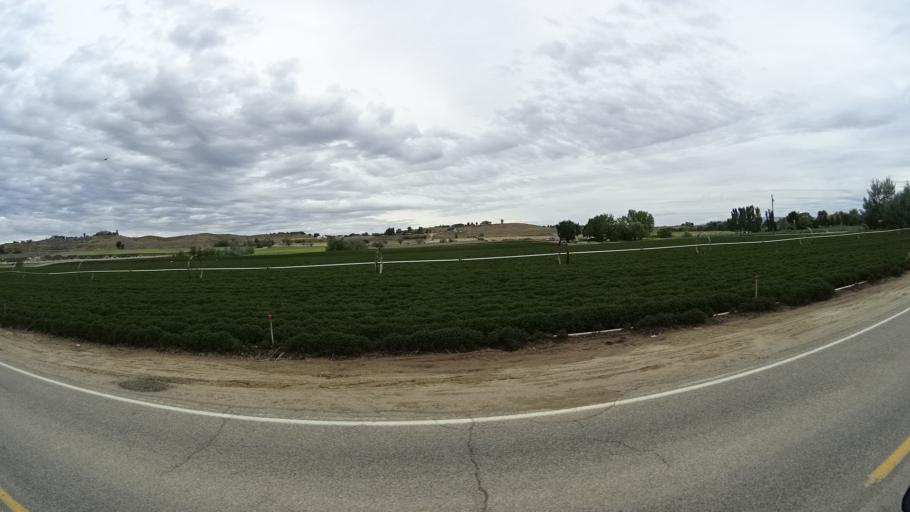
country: US
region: Idaho
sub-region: Ada County
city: Star
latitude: 43.7209
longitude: -116.4795
